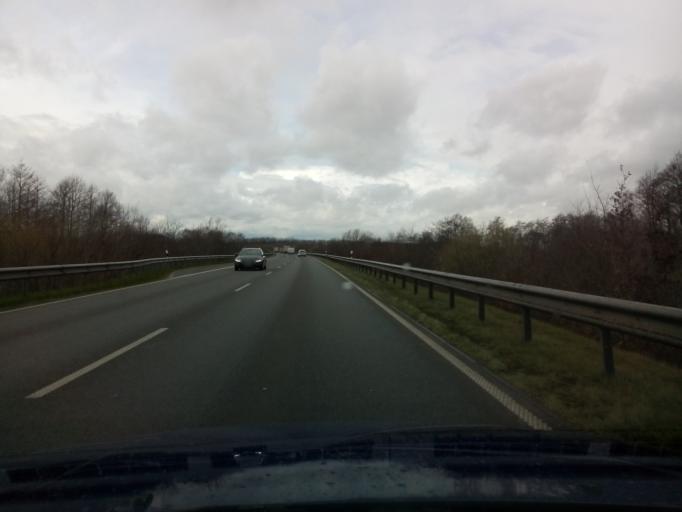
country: DE
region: Lower Saxony
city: Meppen
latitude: 52.7251
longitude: 7.2588
